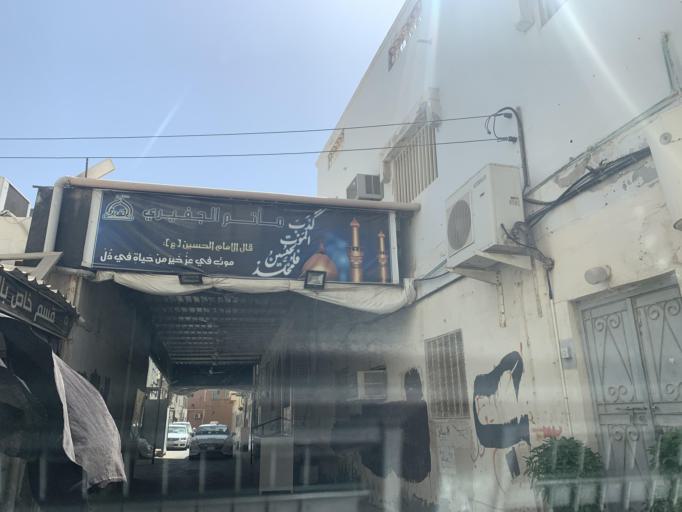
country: BH
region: Northern
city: Sitrah
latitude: 26.1608
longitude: 50.6138
